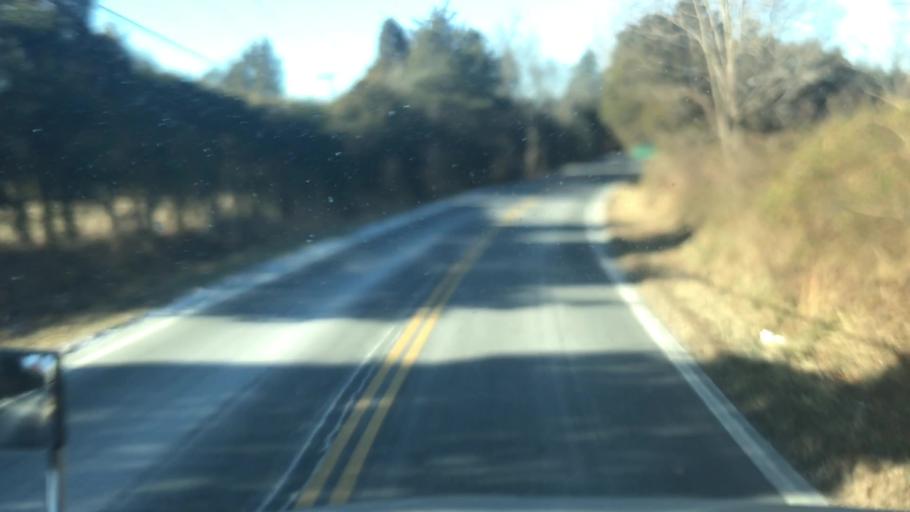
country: US
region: Virginia
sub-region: City of Manassas
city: Manassas
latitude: 38.6920
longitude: -77.5096
